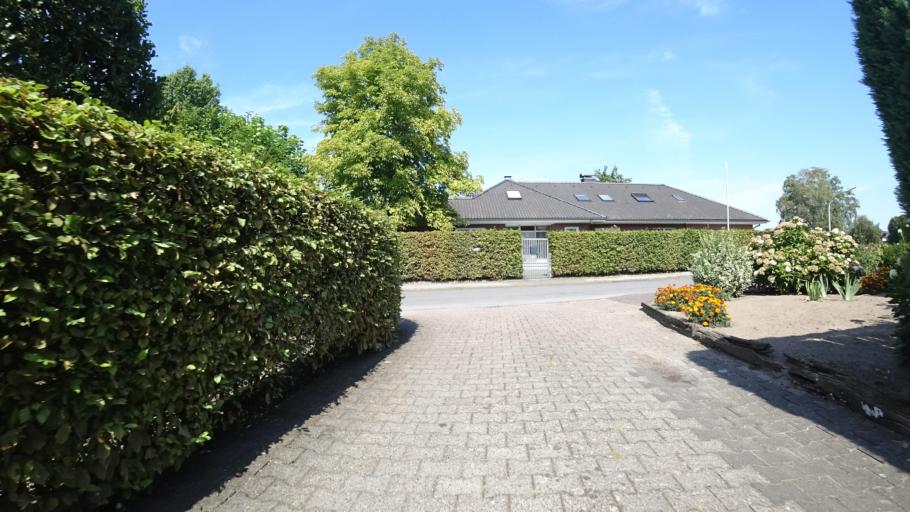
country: DE
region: North Rhine-Westphalia
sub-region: Regierungsbezirk Detmold
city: Rheda-Wiedenbruck
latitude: 51.8595
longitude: 8.2870
